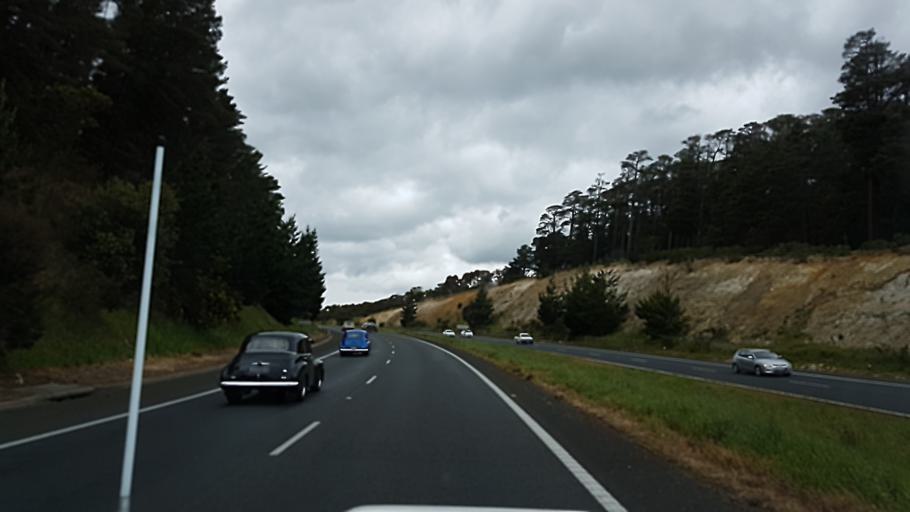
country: AU
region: Victoria
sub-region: Moorabool
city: Bacchus Marsh
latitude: -37.6122
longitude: 144.2995
